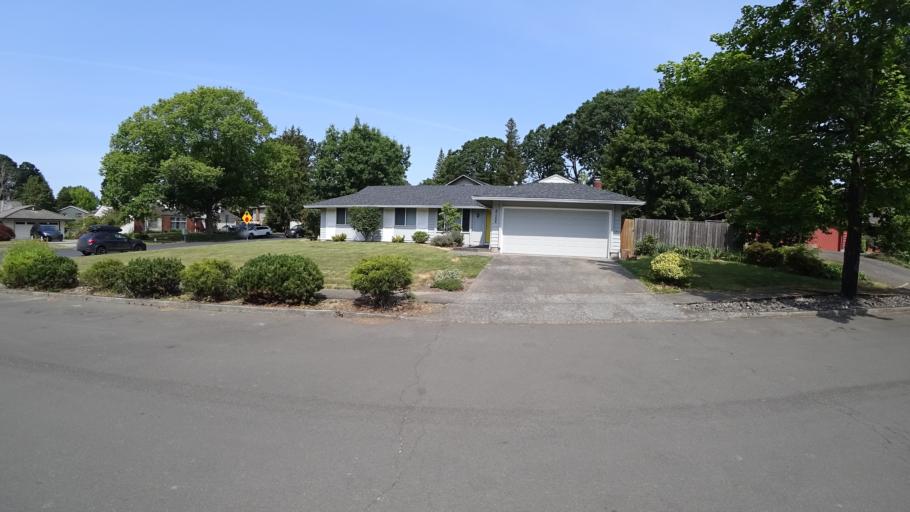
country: US
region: Oregon
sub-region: Washington County
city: Oak Hills
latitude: 45.5354
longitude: -122.8338
